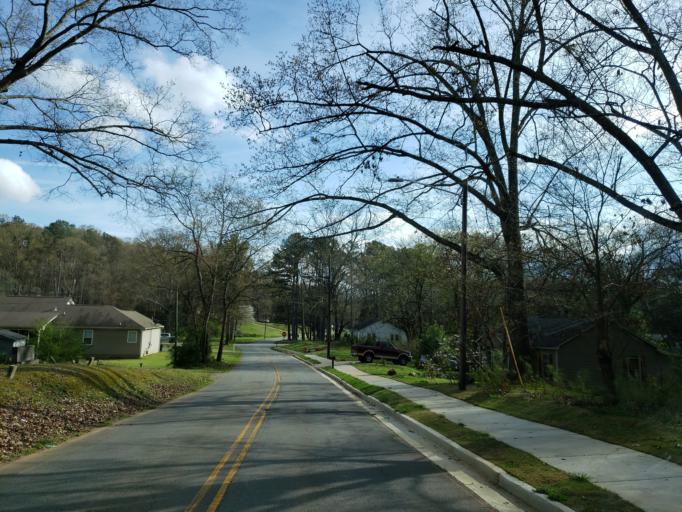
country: US
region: Georgia
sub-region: Bartow County
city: Emerson
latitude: 34.1224
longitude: -84.7582
